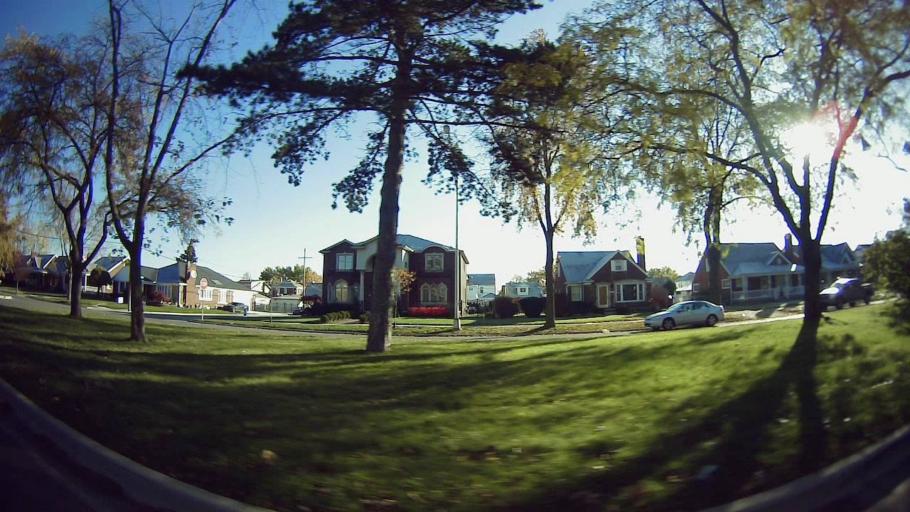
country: US
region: Michigan
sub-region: Wayne County
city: Dearborn
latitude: 42.3312
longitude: -83.1692
